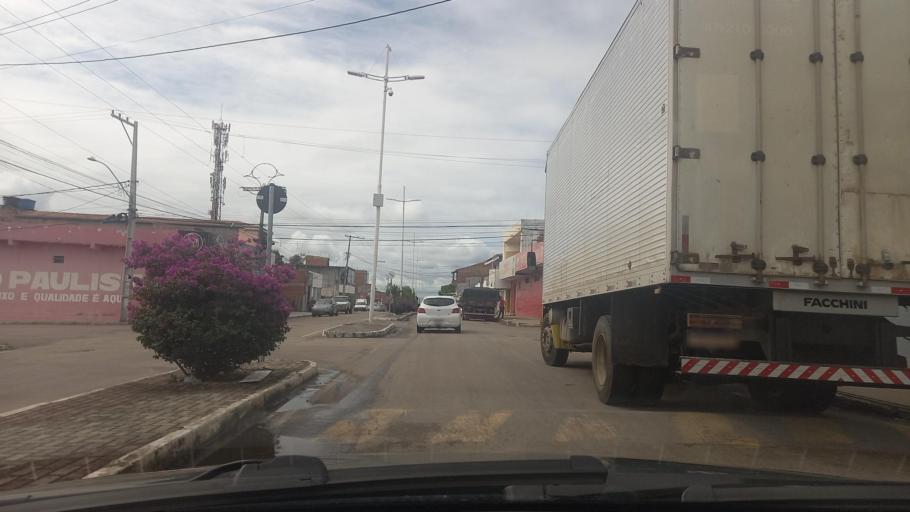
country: BR
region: Bahia
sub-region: Paulo Afonso
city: Paulo Afonso
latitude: -9.4410
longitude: -38.2140
